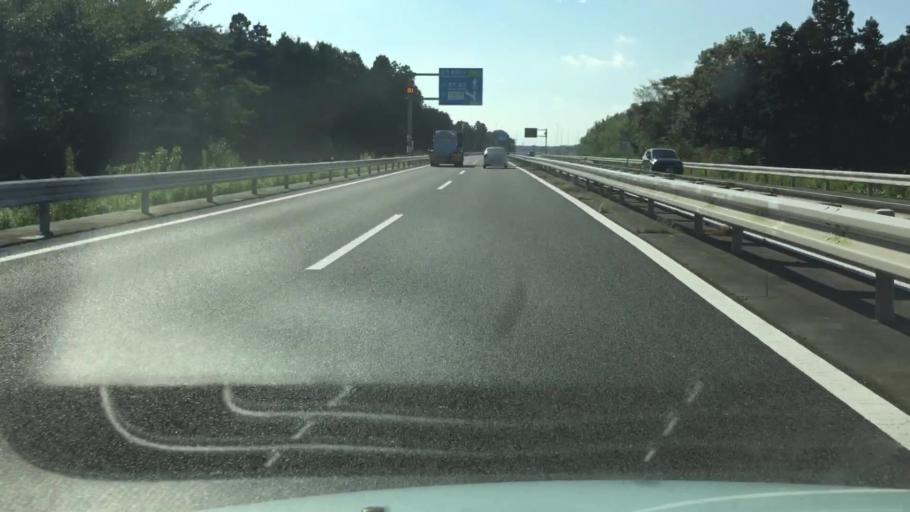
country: JP
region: Tochigi
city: Mooka
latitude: 36.4965
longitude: 139.9902
